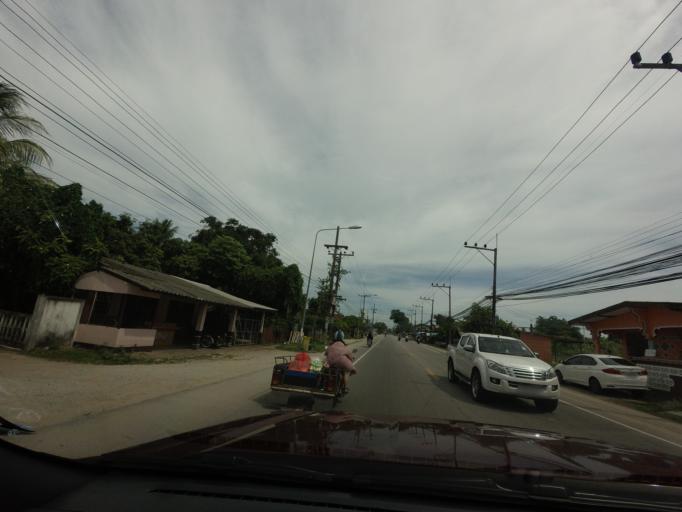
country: TH
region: Narathiwat
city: Tak Bai
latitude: 6.2520
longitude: 102.0644
